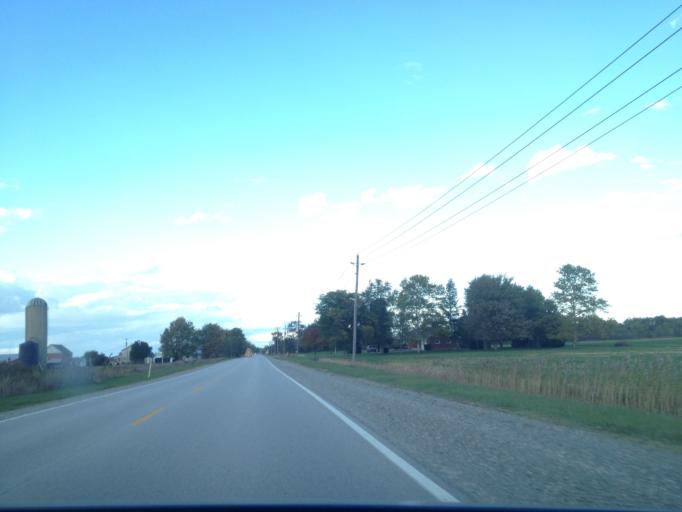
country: US
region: Michigan
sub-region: Wayne County
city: Grosse Pointe
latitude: 42.1543
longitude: -82.7321
